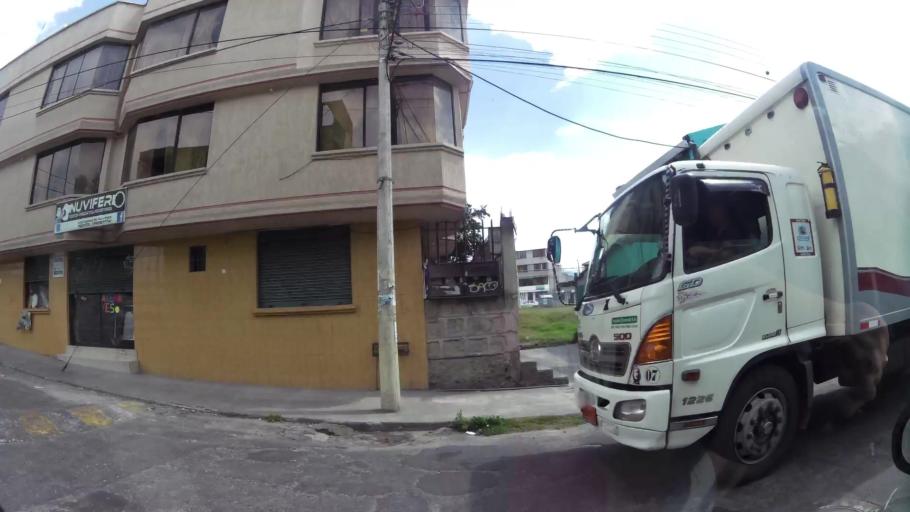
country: EC
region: Pichincha
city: Quito
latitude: -0.0893
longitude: -78.4483
